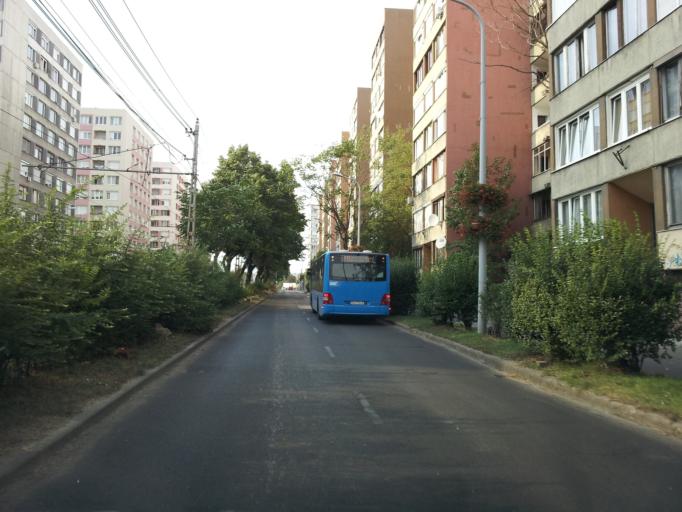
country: HU
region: Budapest
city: Budapest XXII. keruelet
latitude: 47.4309
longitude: 19.0376
